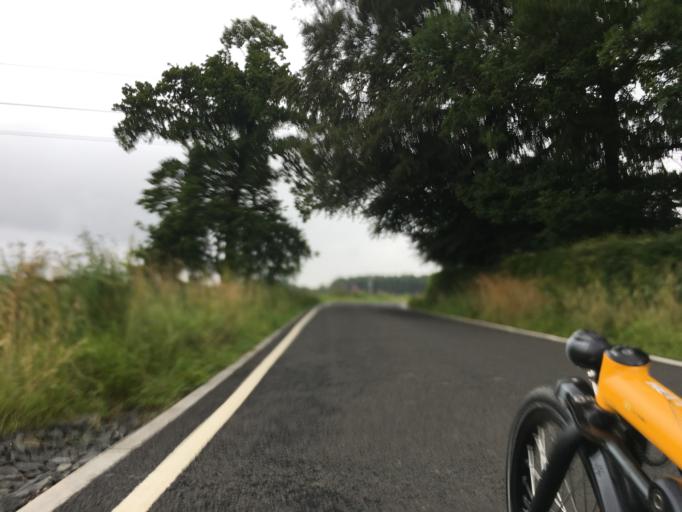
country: GB
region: Scotland
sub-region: West Lothian
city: West Calder
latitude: 55.8405
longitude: -3.5272
